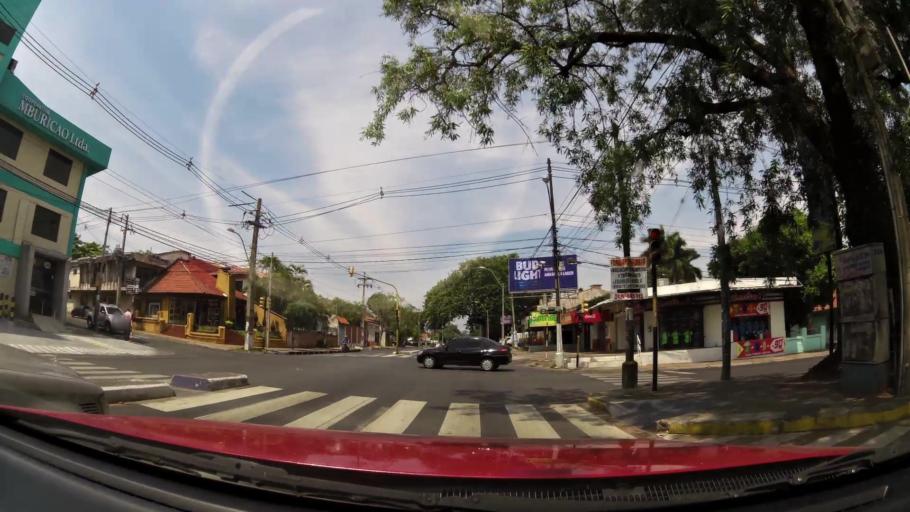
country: PY
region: Asuncion
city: Asuncion
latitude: -25.2945
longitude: -57.5923
